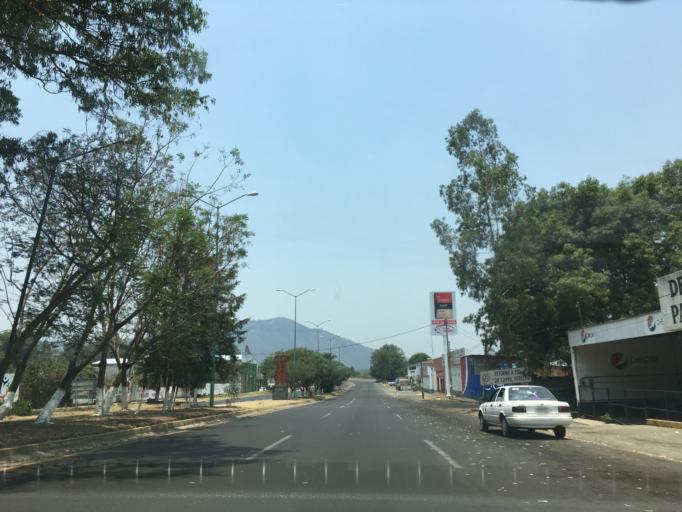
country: MX
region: Michoacan
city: Patzcuaro
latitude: 19.5294
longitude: -101.6112
